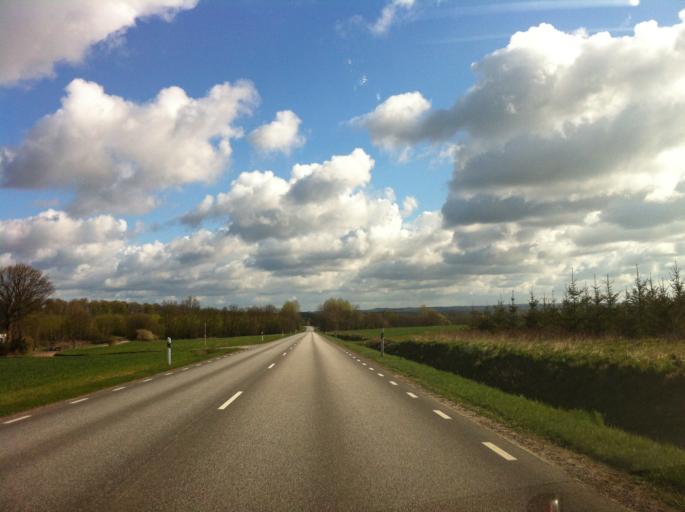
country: SE
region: Skane
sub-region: Eslovs Kommun
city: Stehag
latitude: 55.9181
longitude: 13.3673
